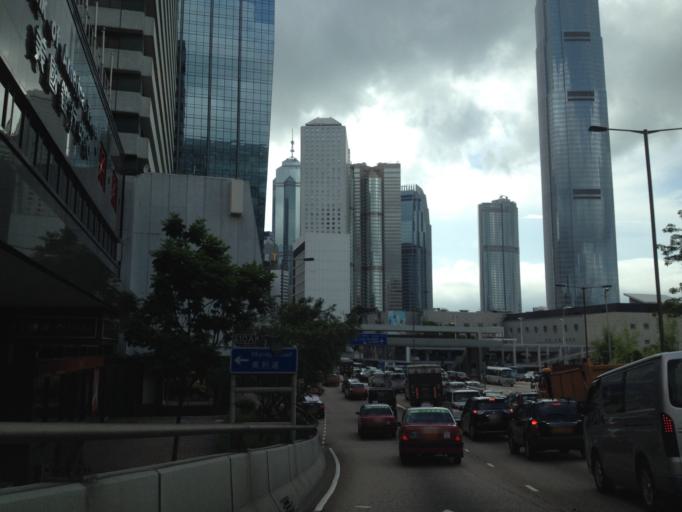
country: HK
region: Central and Western
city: Central
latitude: 22.2810
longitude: 114.1633
